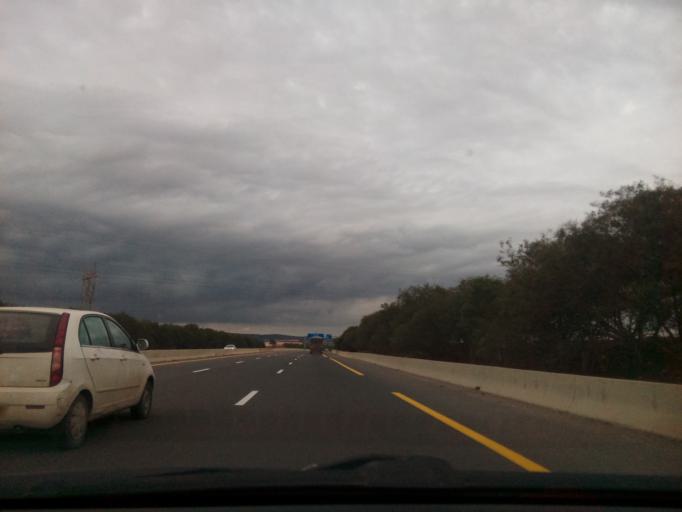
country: DZ
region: Mascara
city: Sig
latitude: 35.5317
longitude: -0.3500
